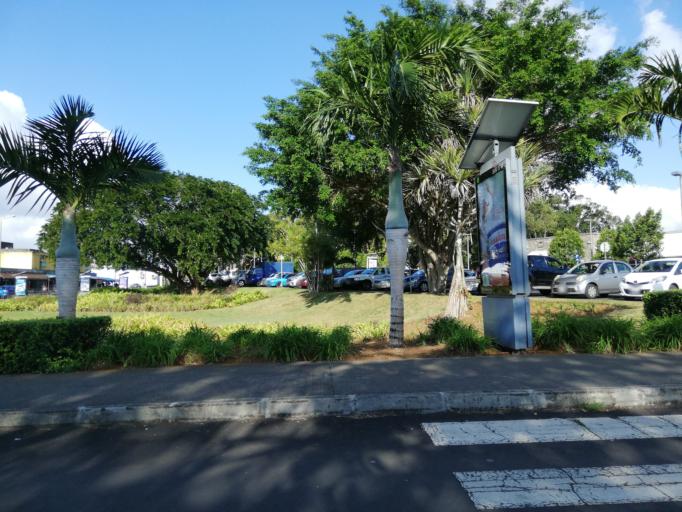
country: MU
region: Moka
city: Verdun
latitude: -20.2254
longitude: 57.5381
